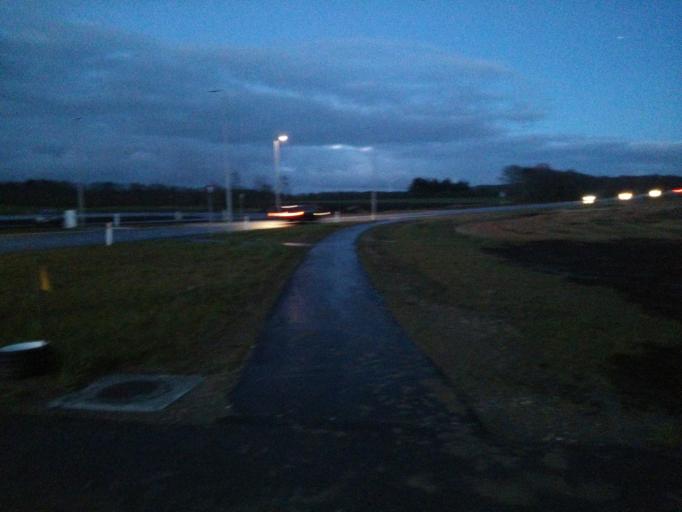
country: DK
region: Central Jutland
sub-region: Herning Kommune
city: Avlum
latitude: 56.2919
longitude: 8.7309
